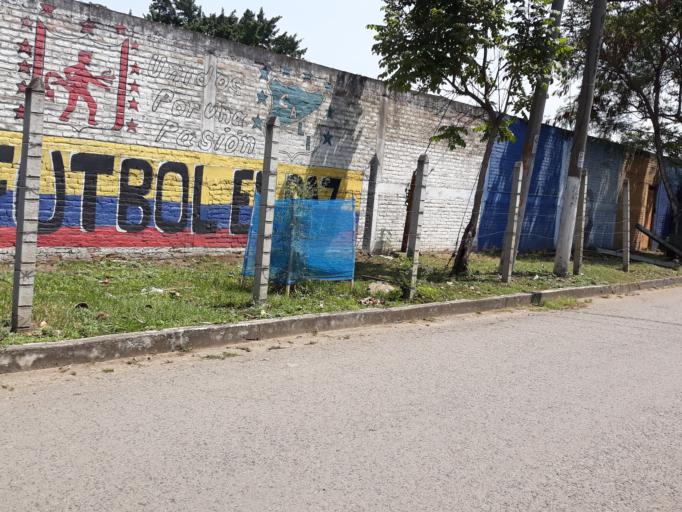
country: CO
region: Valle del Cauca
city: Cali
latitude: 3.4805
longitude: -76.5022
